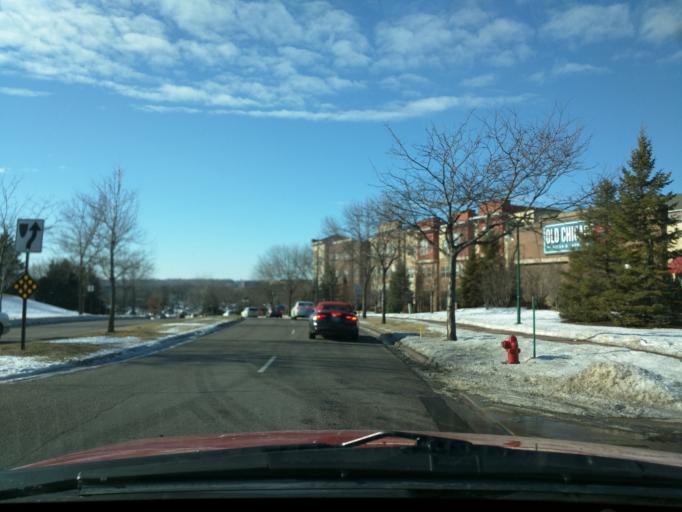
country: US
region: Minnesota
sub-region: Hennepin County
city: Eden Prairie
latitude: 44.8573
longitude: -93.4322
